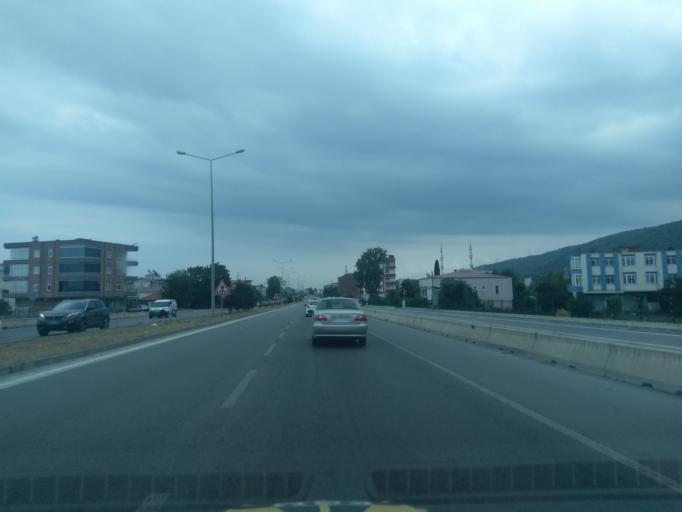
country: TR
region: Samsun
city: Taflan
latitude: 41.4054
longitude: 36.1828
